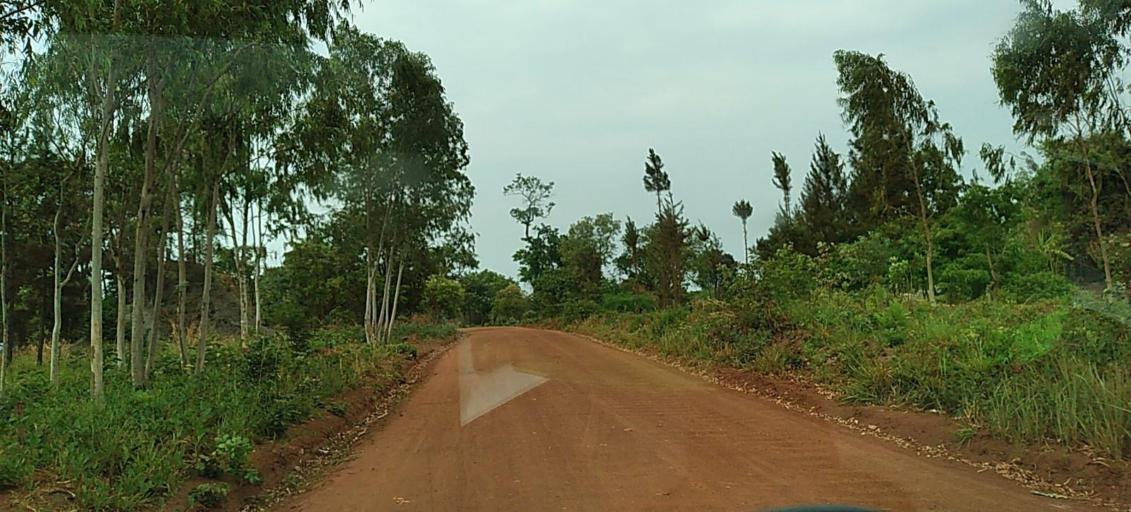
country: ZM
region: North-Western
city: Solwezi
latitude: -12.2330
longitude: 26.5112
